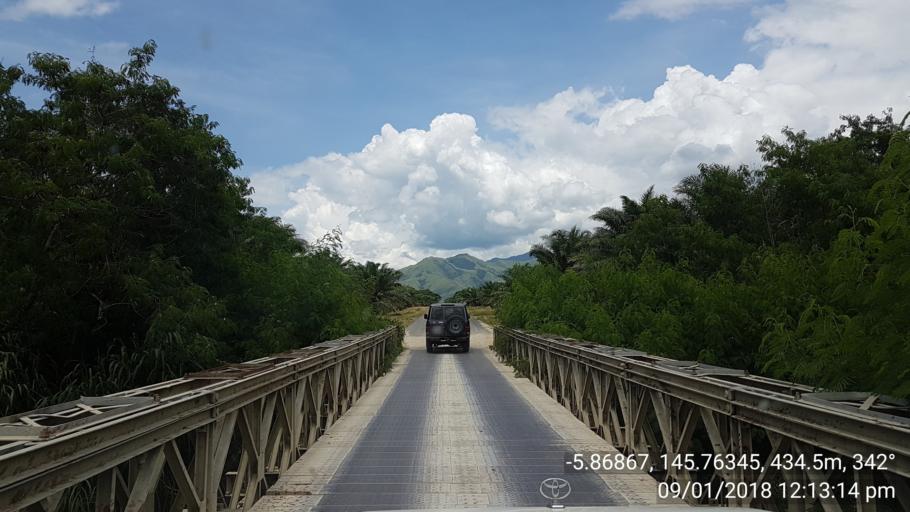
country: PG
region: Eastern Highlands
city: Kainantu
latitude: -5.8686
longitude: 145.7634
